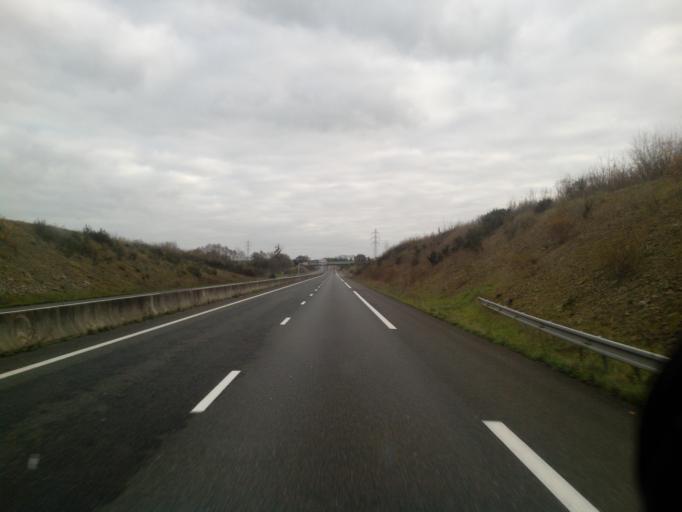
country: FR
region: Poitou-Charentes
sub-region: Departement des Deux-Sevres
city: Saint-Pierre-des-Echaubrognes
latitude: 46.9412
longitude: -0.7535
